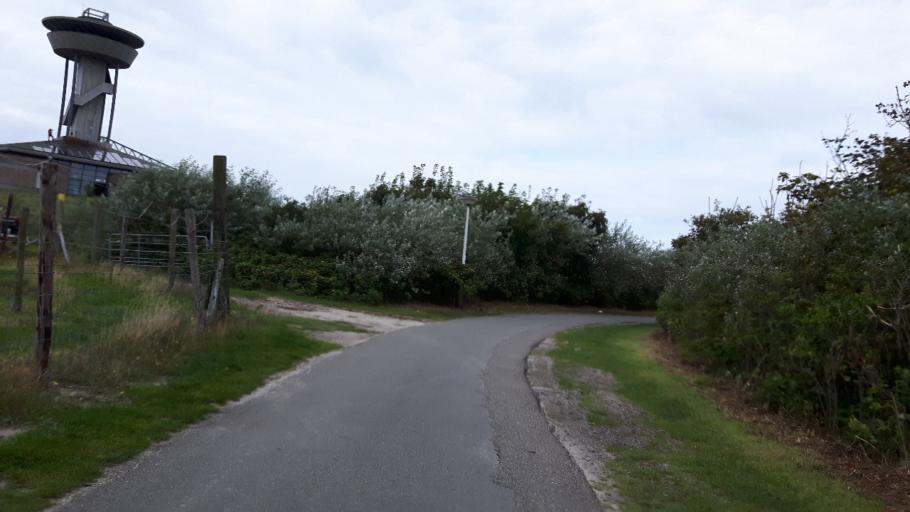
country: NL
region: Friesland
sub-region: Gemeente Ameland
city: Nes
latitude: 53.4487
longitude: 5.7753
